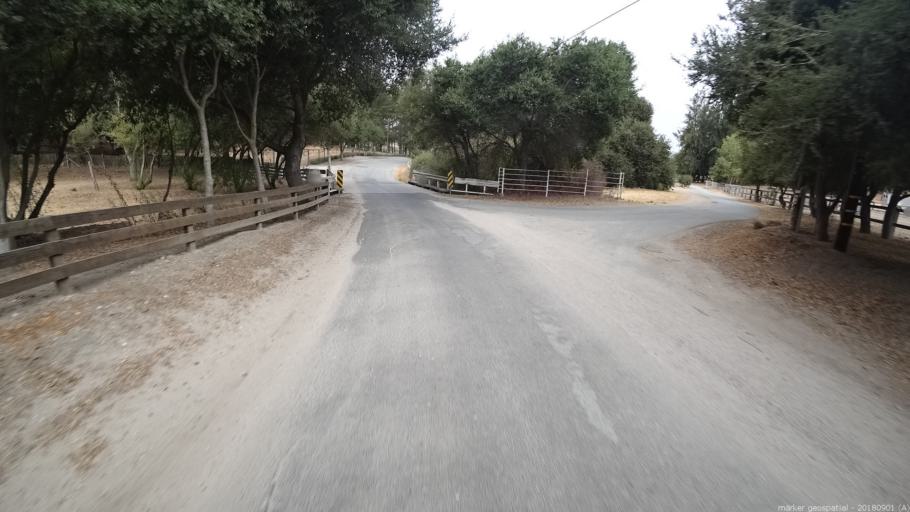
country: US
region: California
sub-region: Monterey County
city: Greenfield
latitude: 36.2721
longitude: -121.3010
